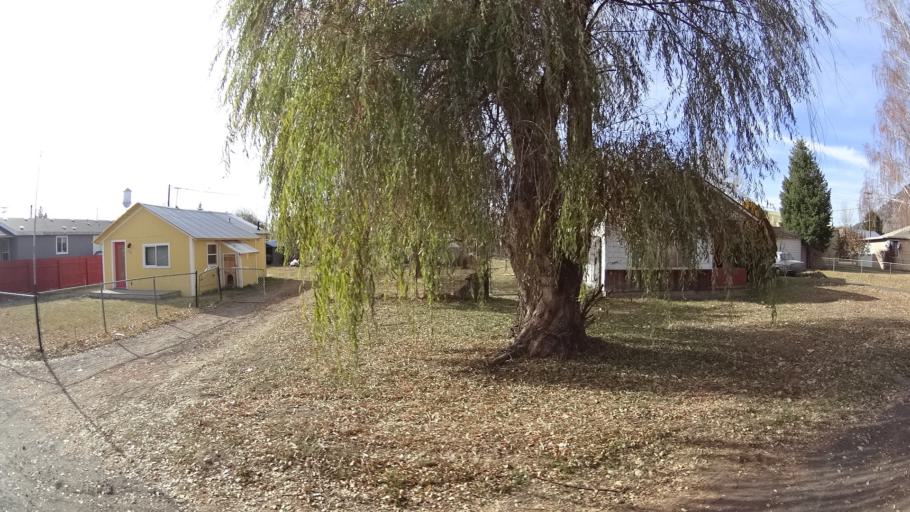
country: US
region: Oregon
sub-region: Klamath County
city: Klamath Falls
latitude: 41.9681
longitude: -121.9170
